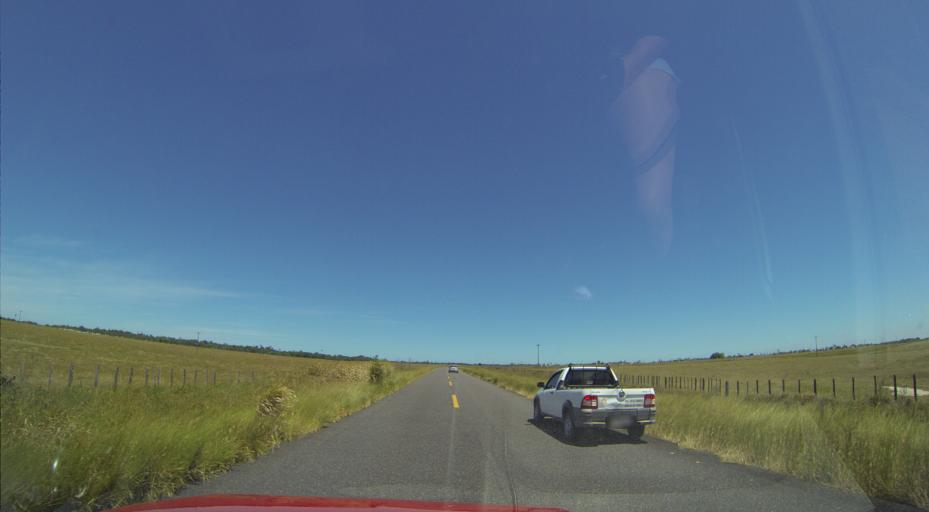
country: BR
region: Bahia
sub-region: Prado
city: Prado
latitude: -17.2373
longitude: -39.3661
